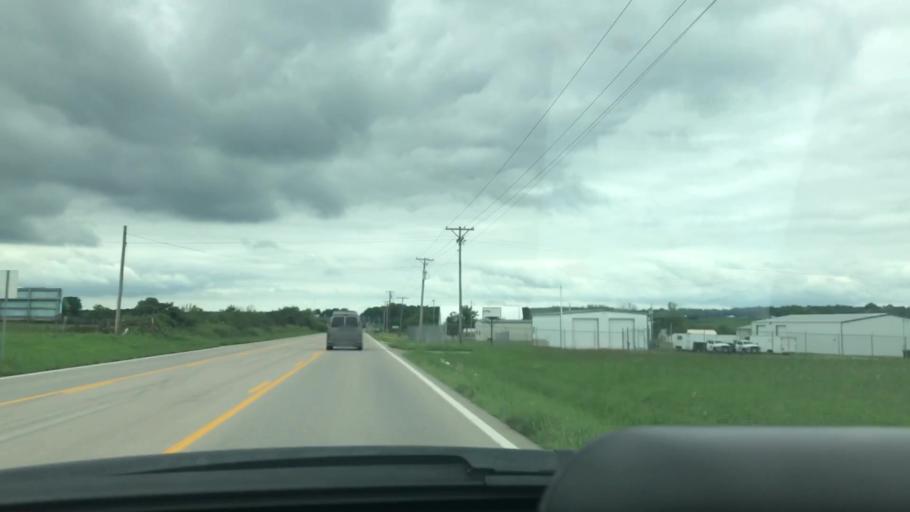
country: US
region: Missouri
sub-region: Dallas County
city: Buffalo
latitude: 37.6580
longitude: -93.1036
